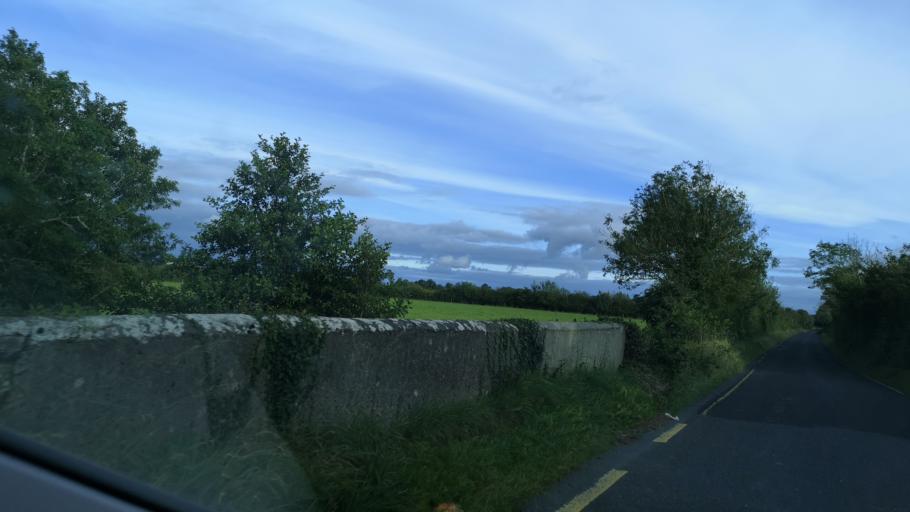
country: IE
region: Connaught
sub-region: County Galway
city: Ballinasloe
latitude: 53.3422
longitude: -8.2944
